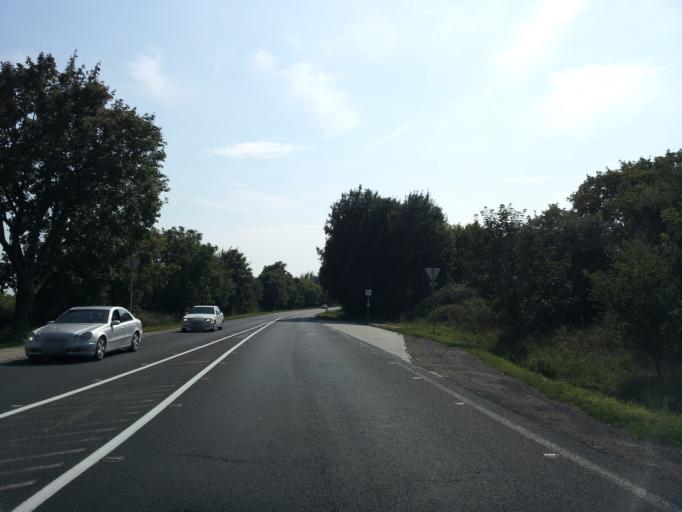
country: HU
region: Fejer
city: Lepseny
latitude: 46.9712
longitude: 18.2051
